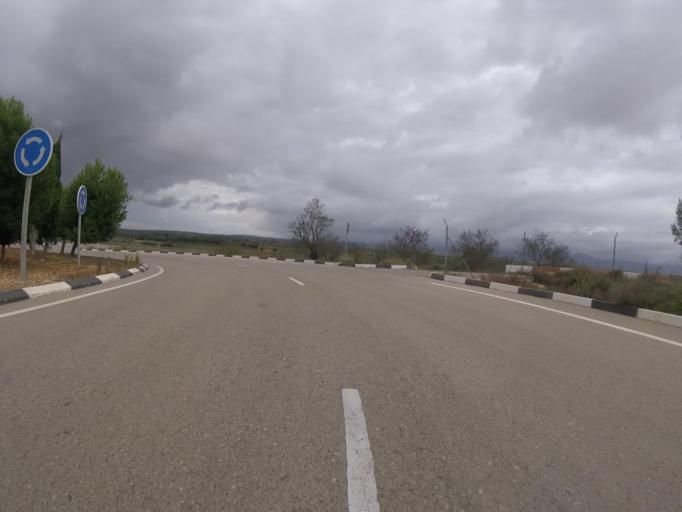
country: ES
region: Valencia
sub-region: Provincia de Castello
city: Benlloch
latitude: 40.1965
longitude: 0.0530
